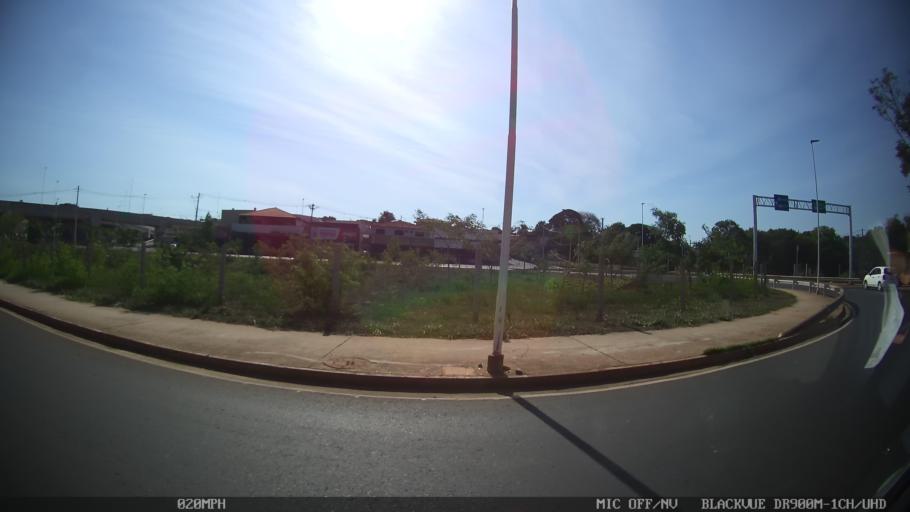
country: BR
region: Sao Paulo
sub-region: Sao Jose Do Rio Preto
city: Sao Jose do Rio Preto
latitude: -20.7886
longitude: -49.3876
